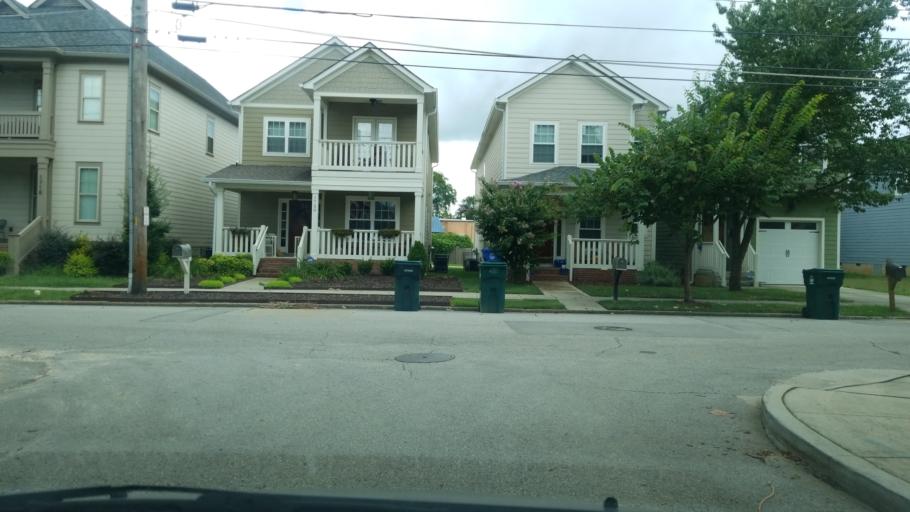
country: US
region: Tennessee
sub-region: Hamilton County
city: Chattanooga
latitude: 35.0340
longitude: -85.3098
